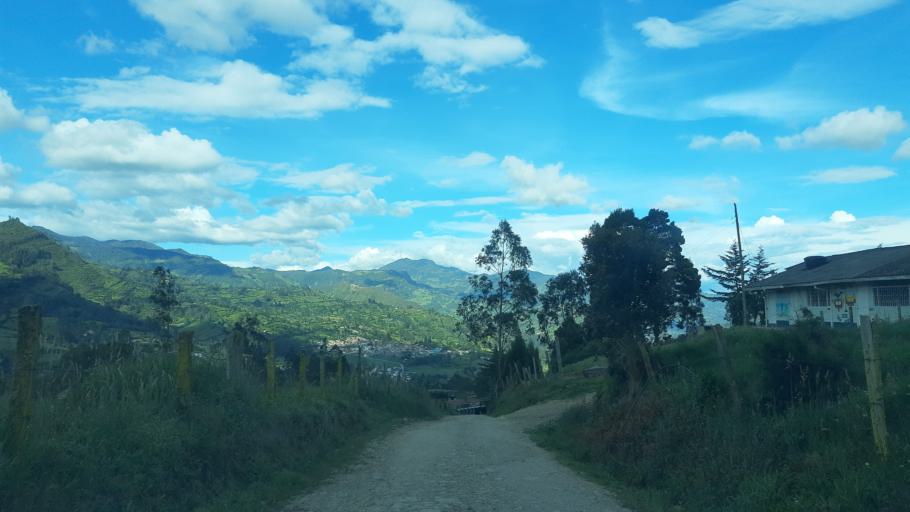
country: CO
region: Cundinamarca
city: Macheta
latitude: 5.0698
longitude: -73.6294
